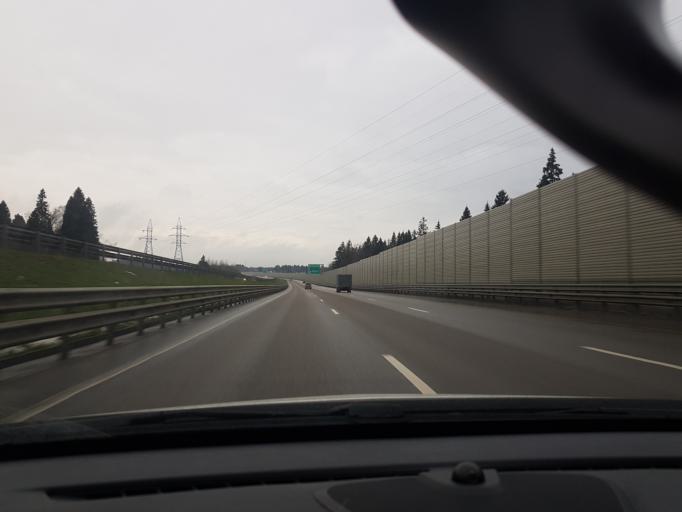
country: RU
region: Moskovskaya
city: Novopetrovskoye
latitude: 55.9711
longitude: 36.4894
